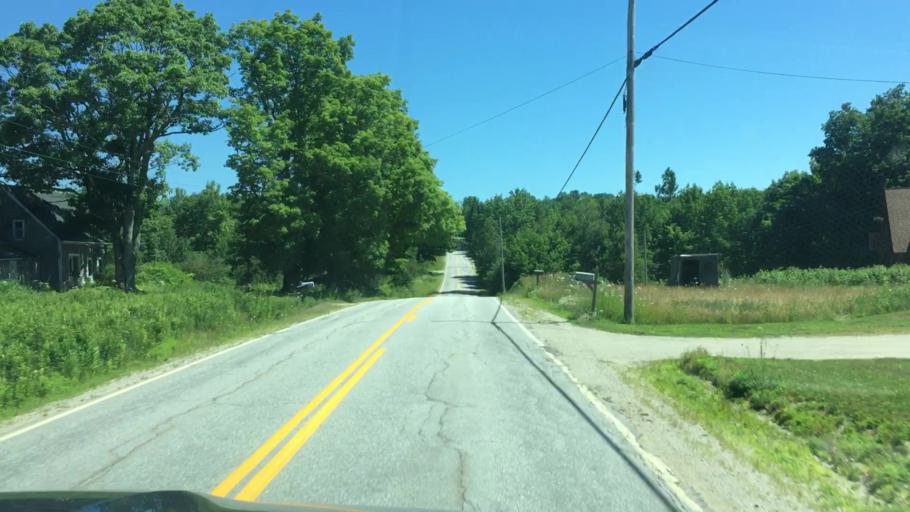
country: US
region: Maine
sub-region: Hancock County
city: Penobscot
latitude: 44.5192
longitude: -68.6660
